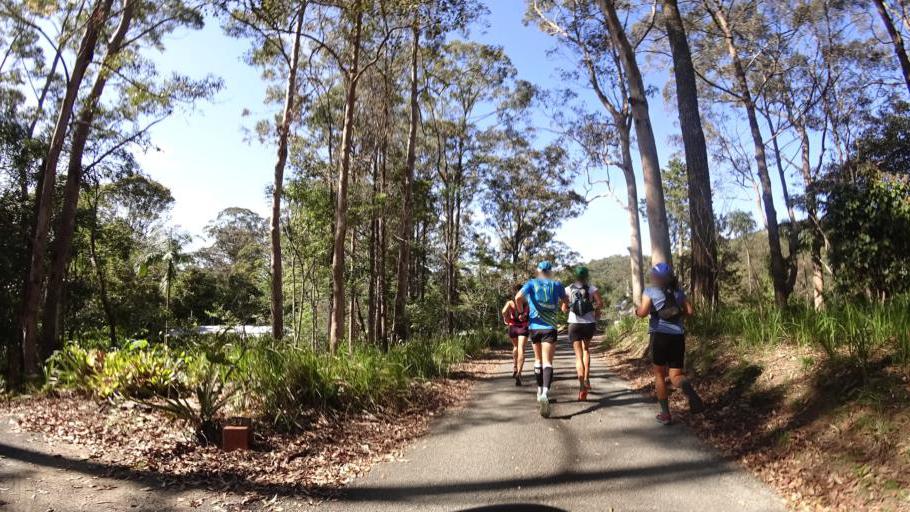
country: AU
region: Queensland
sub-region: Moreton Bay
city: Highvale
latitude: -27.4002
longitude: 152.7824
